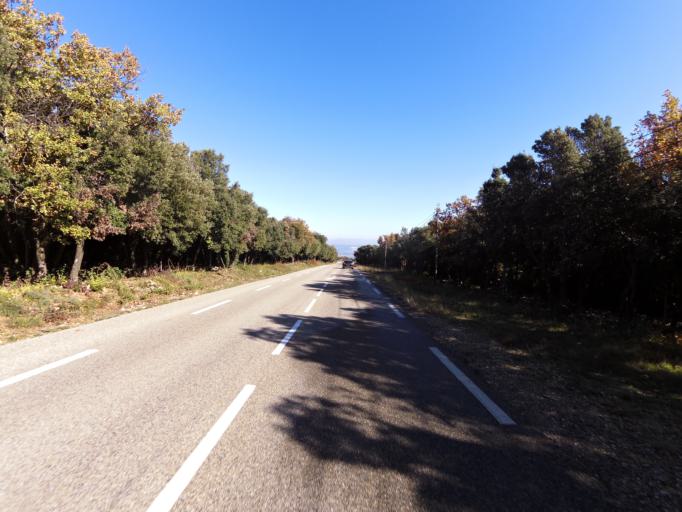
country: FR
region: Rhone-Alpes
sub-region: Departement de l'Ardeche
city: Bourg-Saint-Andeol
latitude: 44.4020
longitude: 4.6022
